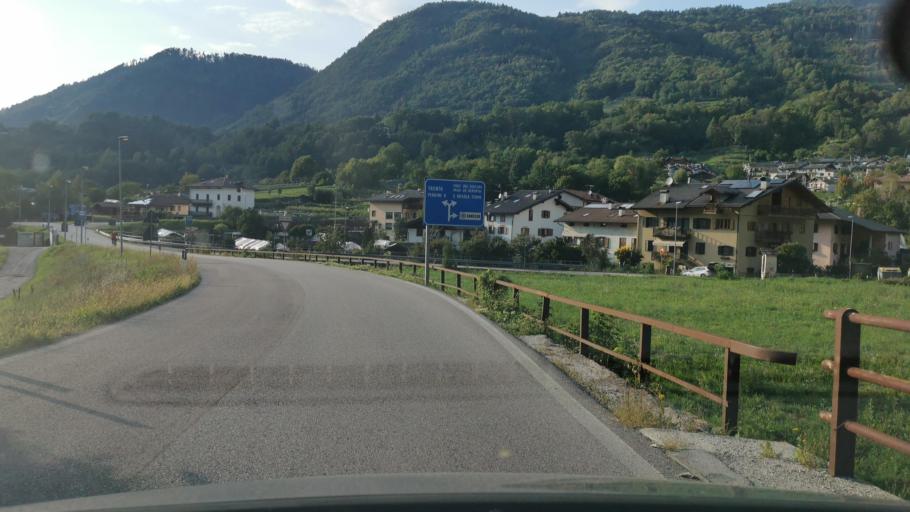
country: IT
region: Trentino-Alto Adige
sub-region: Provincia di Trento
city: Frassilongo
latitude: 46.0765
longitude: 11.2768
